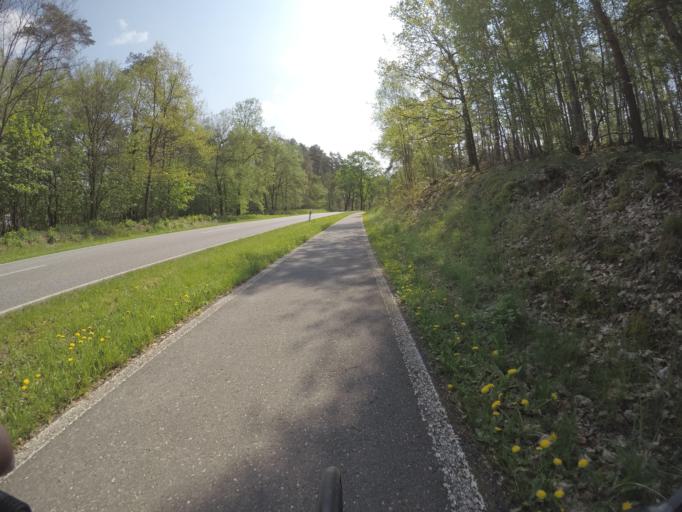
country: DE
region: Brandenburg
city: Wandlitz
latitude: 52.7962
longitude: 13.5174
